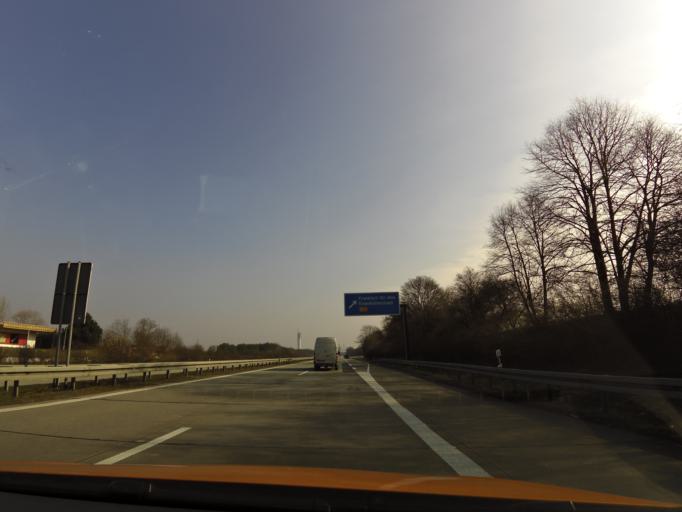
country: DE
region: Brandenburg
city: Frankfurt (Oder)
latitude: 52.3197
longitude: 14.5095
